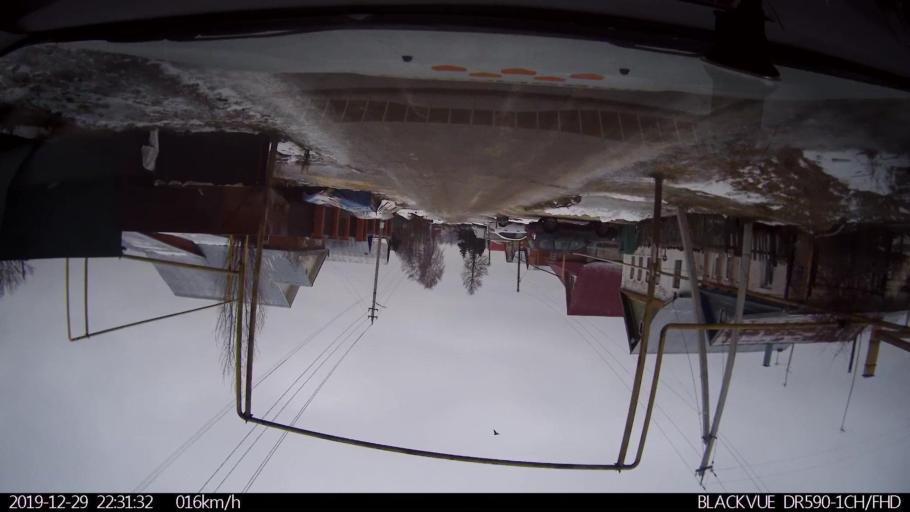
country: RU
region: Nizjnij Novgorod
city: Afonino
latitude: 56.2027
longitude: 43.9860
